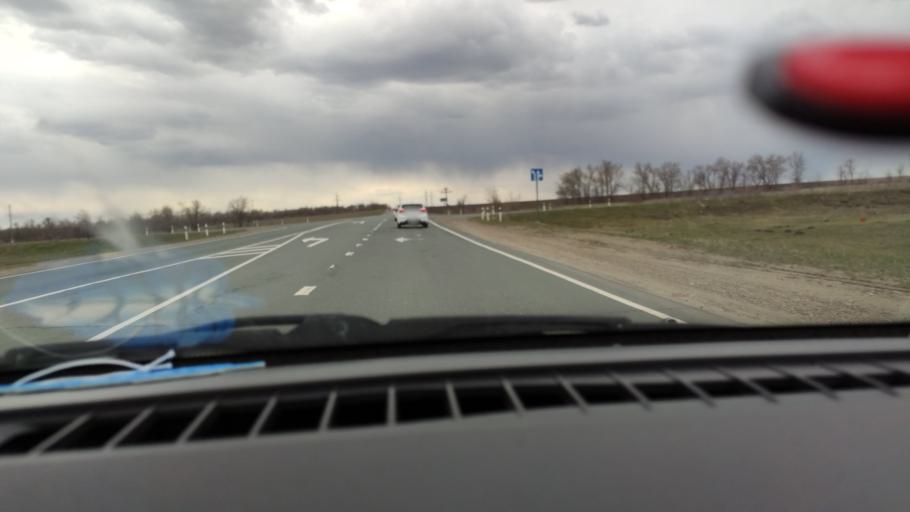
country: RU
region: Saratov
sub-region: Saratovskiy Rayon
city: Saratov
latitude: 51.7508
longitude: 46.0599
